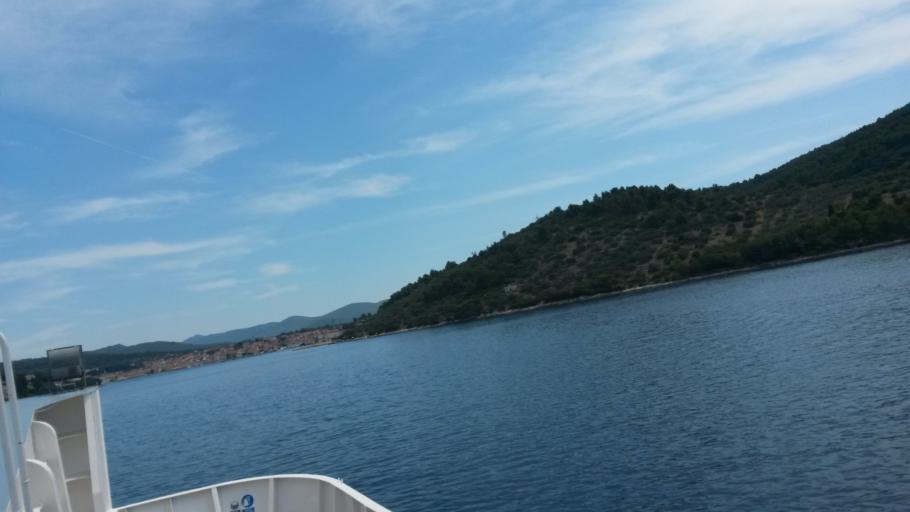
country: HR
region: Dubrovacko-Neretvanska
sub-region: Grad Dubrovnik
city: Vela Luka
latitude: 42.9626
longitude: 16.6936
